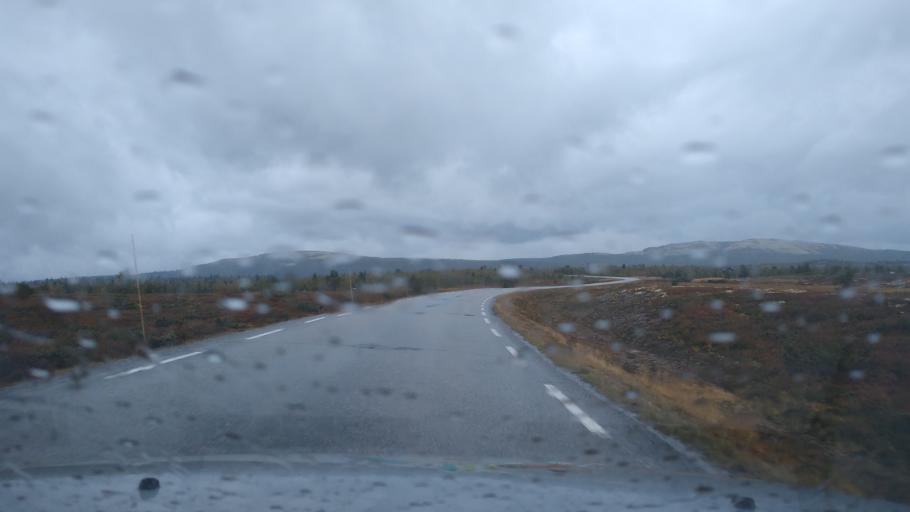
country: NO
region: Oppland
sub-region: Ringebu
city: Ringebu
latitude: 61.6638
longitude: 10.1239
